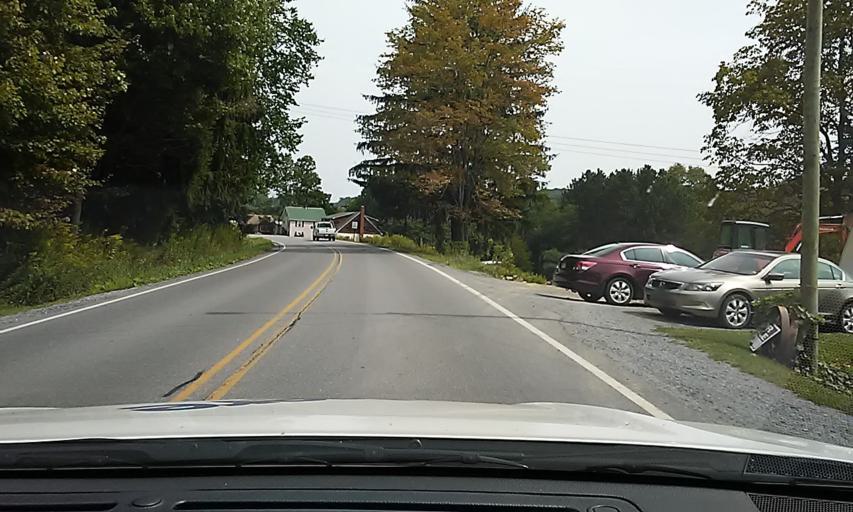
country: US
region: Pennsylvania
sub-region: Elk County
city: Saint Marys
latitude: 41.3220
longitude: -78.6362
